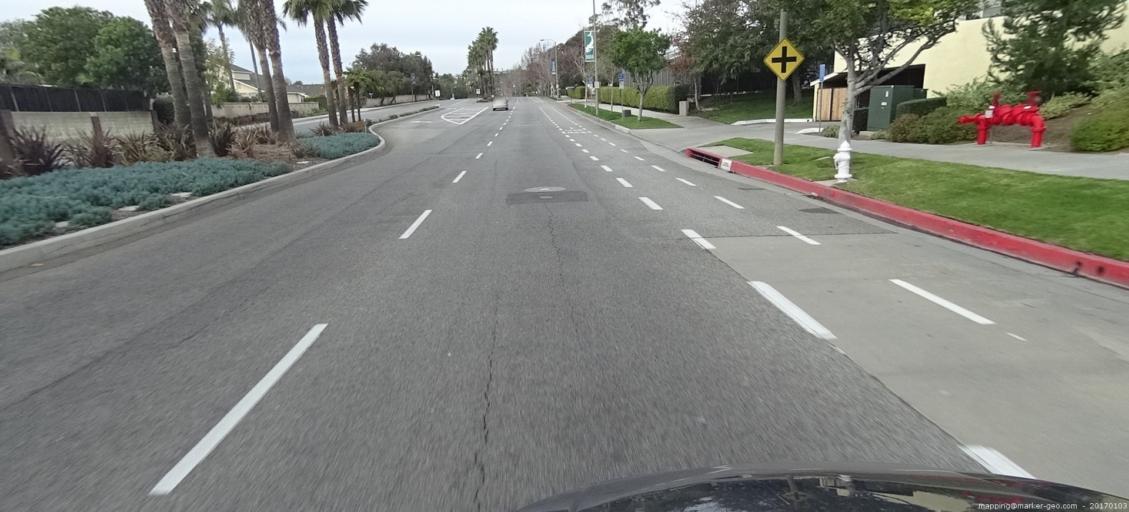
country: US
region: California
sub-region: Orange County
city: Dana Point
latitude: 33.4797
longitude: -117.6976
